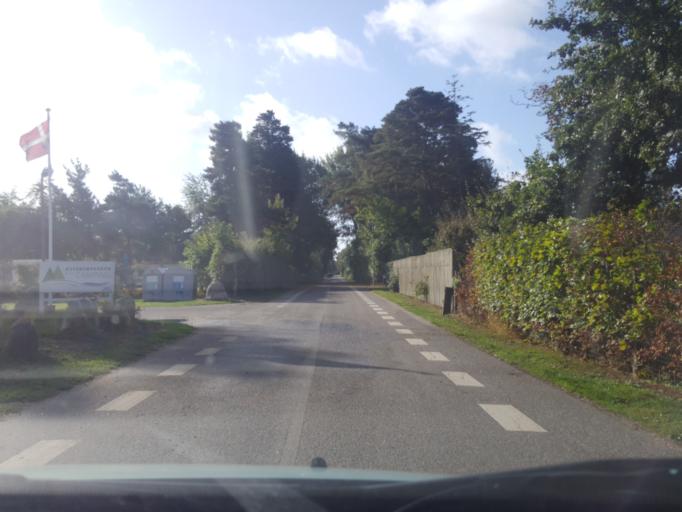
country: DK
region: Zealand
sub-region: Guldborgsund Kommune
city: Nykobing Falster
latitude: 54.6562
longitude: 11.9565
